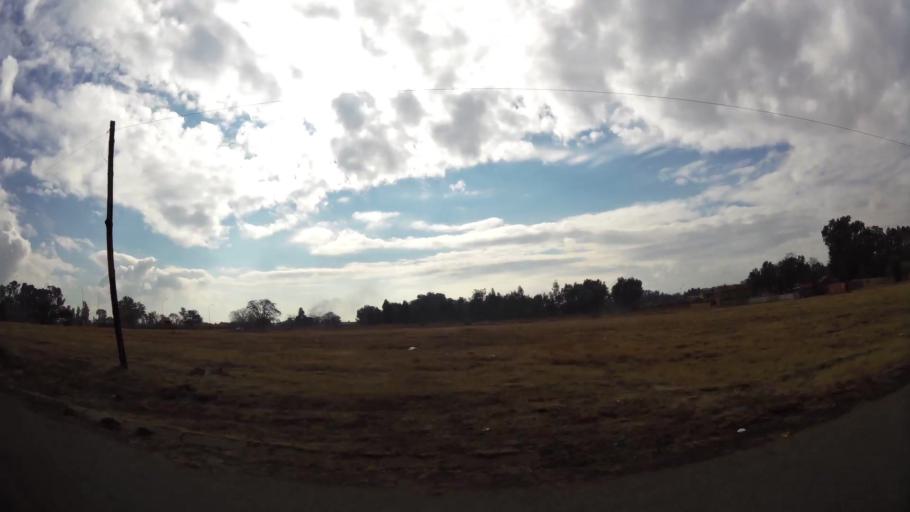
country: ZA
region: Gauteng
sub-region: Sedibeng District Municipality
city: Meyerton
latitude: -26.5875
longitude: 28.0062
